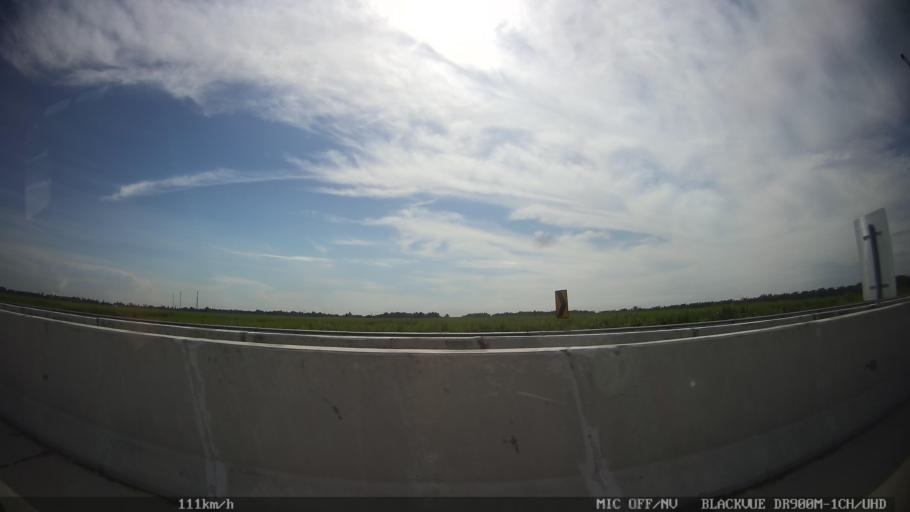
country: ID
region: North Sumatra
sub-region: Kabupaten Langkat
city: Stabat
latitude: 3.6920
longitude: 98.5402
